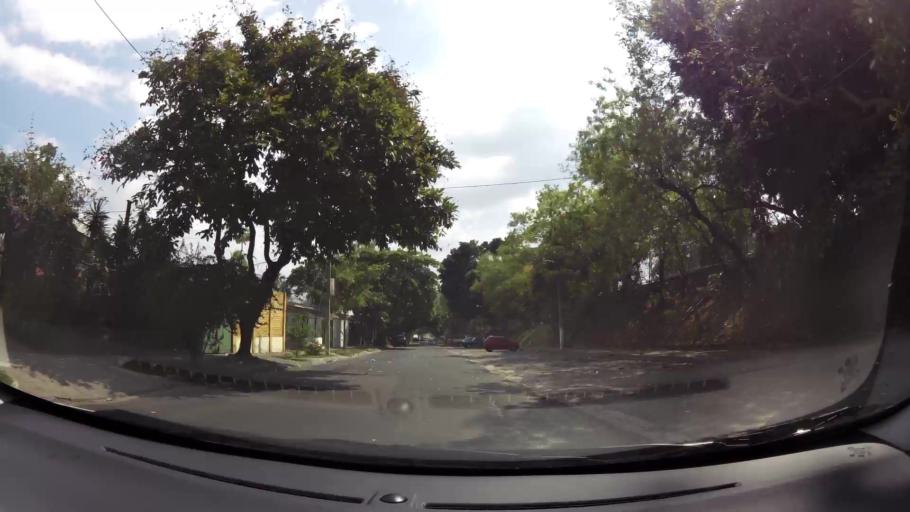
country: SV
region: San Salvador
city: Mejicanos
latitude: 13.7098
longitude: -89.2151
